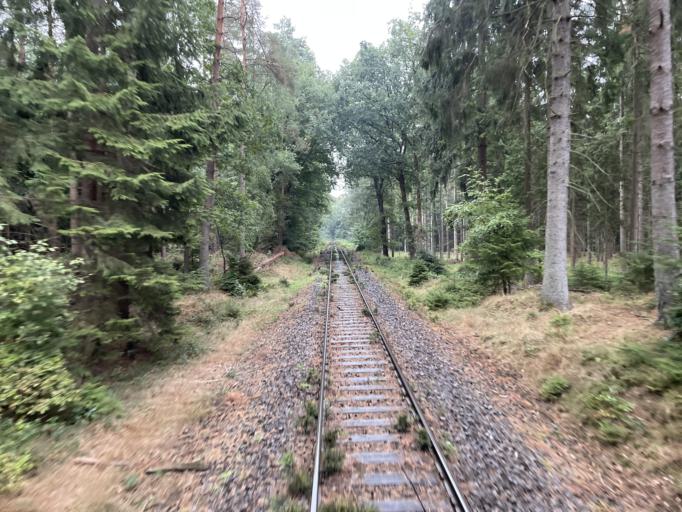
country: DE
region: Lower Saxony
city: Betzendorf
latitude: 53.1519
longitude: 10.3341
